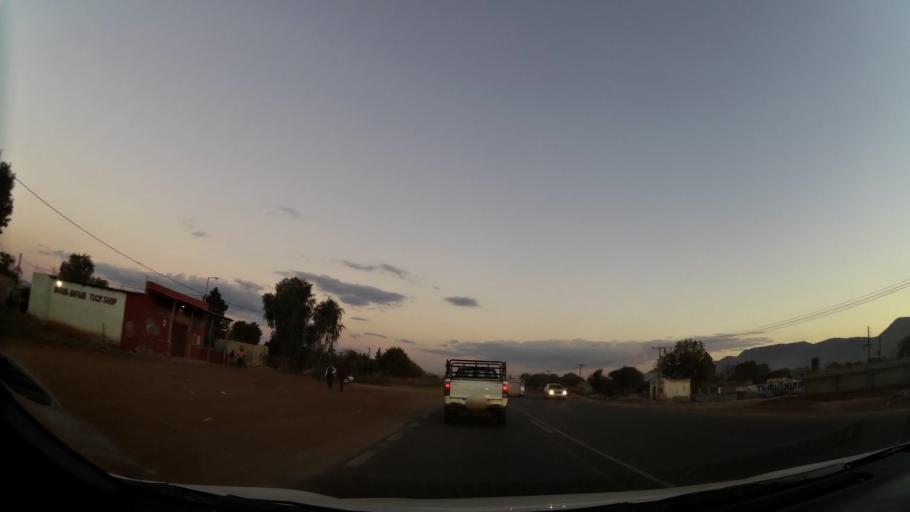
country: ZA
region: Limpopo
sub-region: Waterberg District Municipality
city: Mokopane
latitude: -24.1676
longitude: 28.9846
